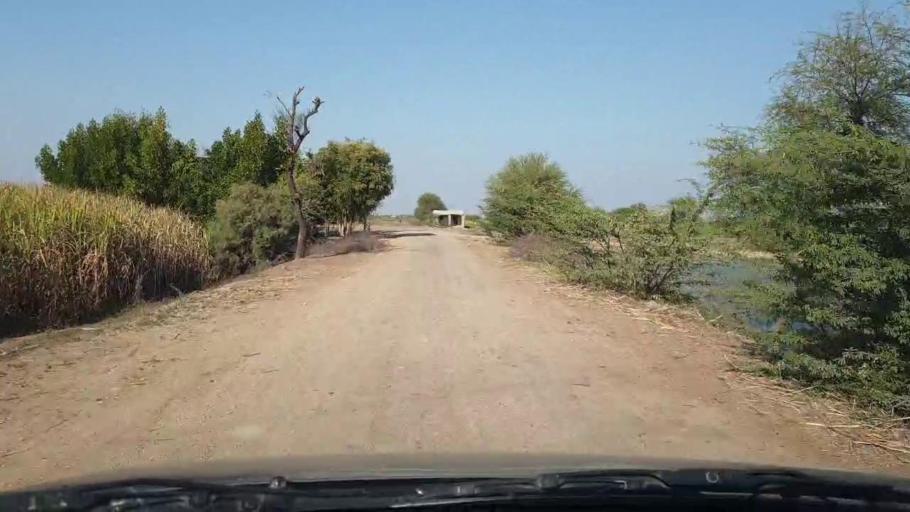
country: PK
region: Sindh
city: Samaro
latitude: 25.1702
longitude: 69.2855
